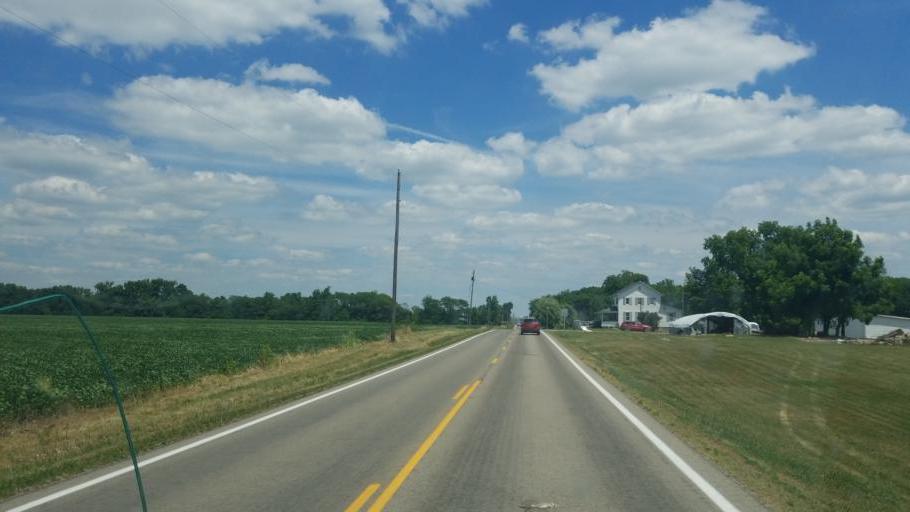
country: US
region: Ohio
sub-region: Defiance County
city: Hicksville
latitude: 41.2731
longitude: -84.7998
